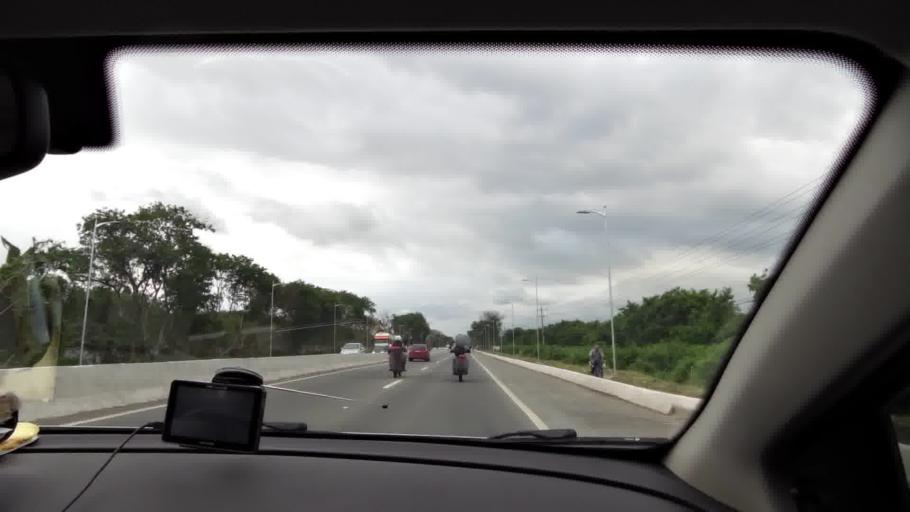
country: BR
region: Espirito Santo
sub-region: Vila Velha
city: Vila Velha
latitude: -20.2447
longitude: -40.2828
